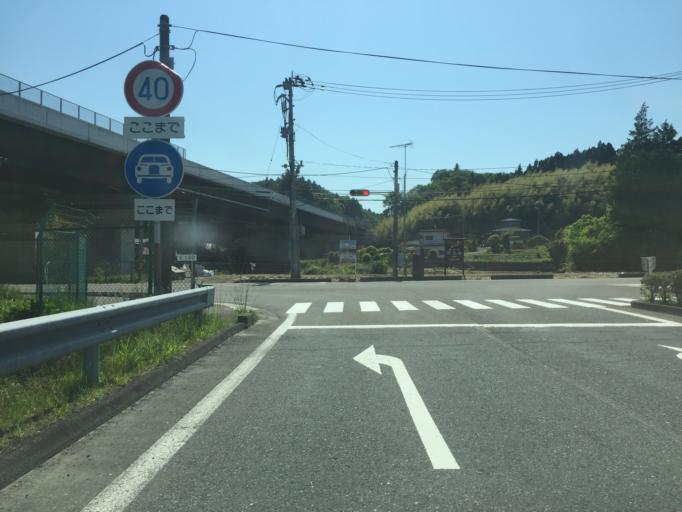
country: JP
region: Miyagi
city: Matsushima
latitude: 38.4005
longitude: 141.0679
